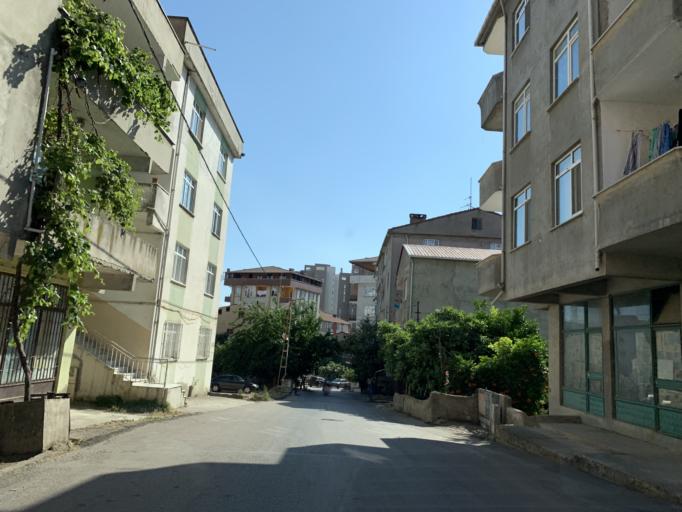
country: TR
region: Istanbul
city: Pendik
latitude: 40.8731
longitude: 29.2799
